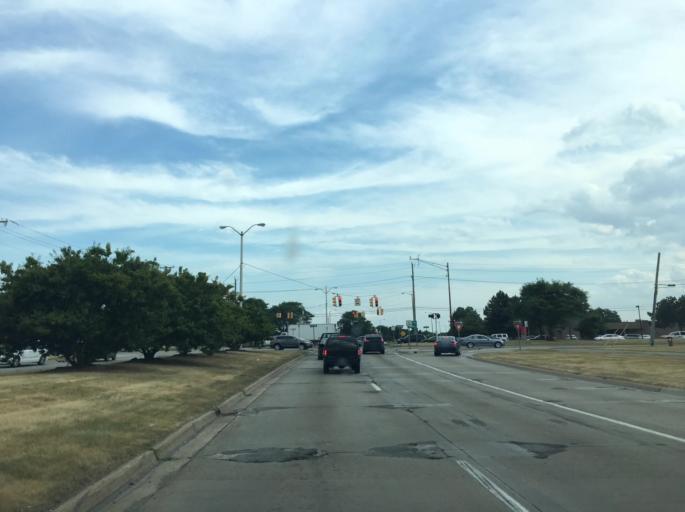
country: US
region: Michigan
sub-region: Macomb County
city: Sterling Heights
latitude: 42.5680
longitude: -82.9882
